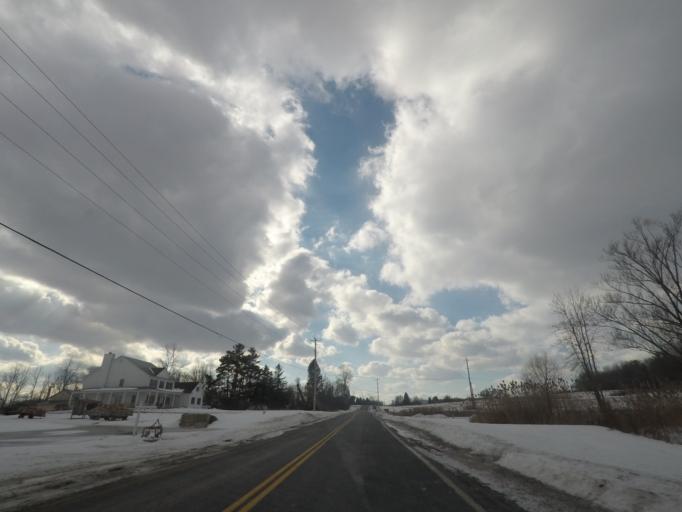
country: US
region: New York
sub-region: Saratoga County
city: Mechanicville
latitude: 42.9139
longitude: -73.7426
